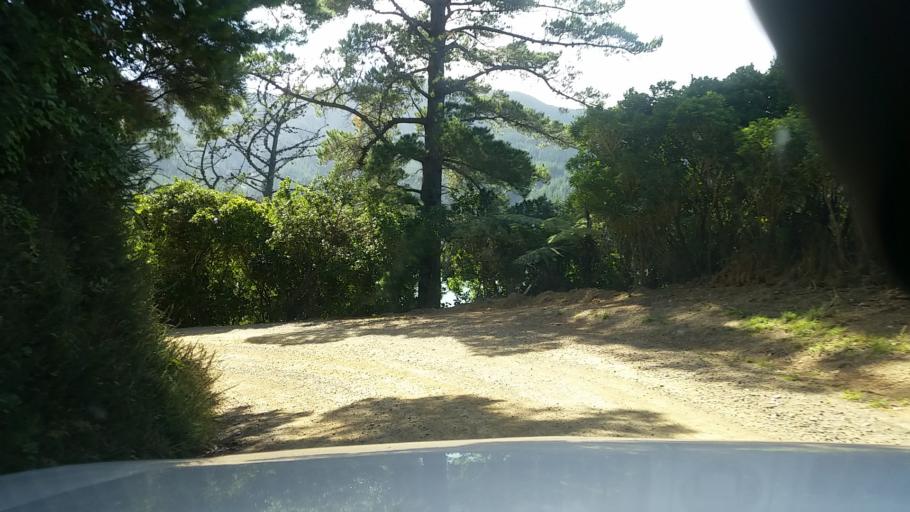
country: NZ
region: Marlborough
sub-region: Marlborough District
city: Picton
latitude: -41.2878
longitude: 174.1754
